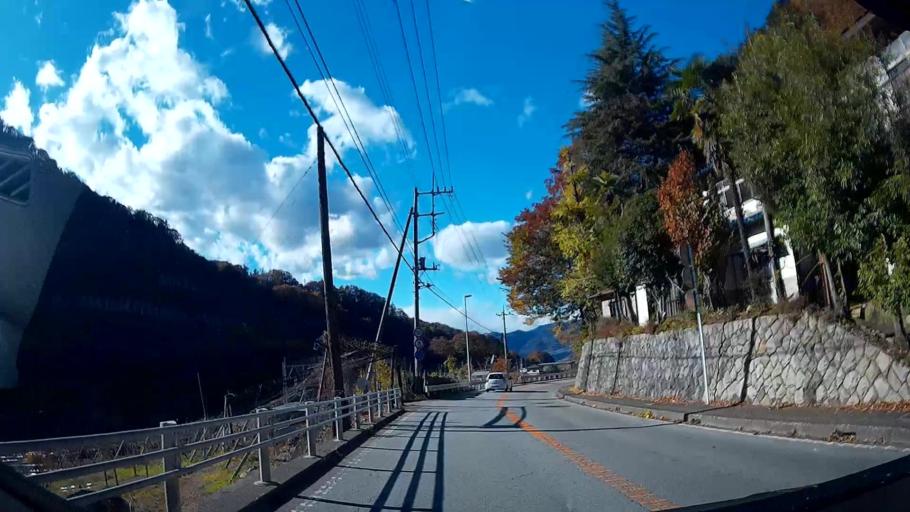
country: JP
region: Yamanashi
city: Enzan
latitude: 35.6483
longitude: 138.7595
